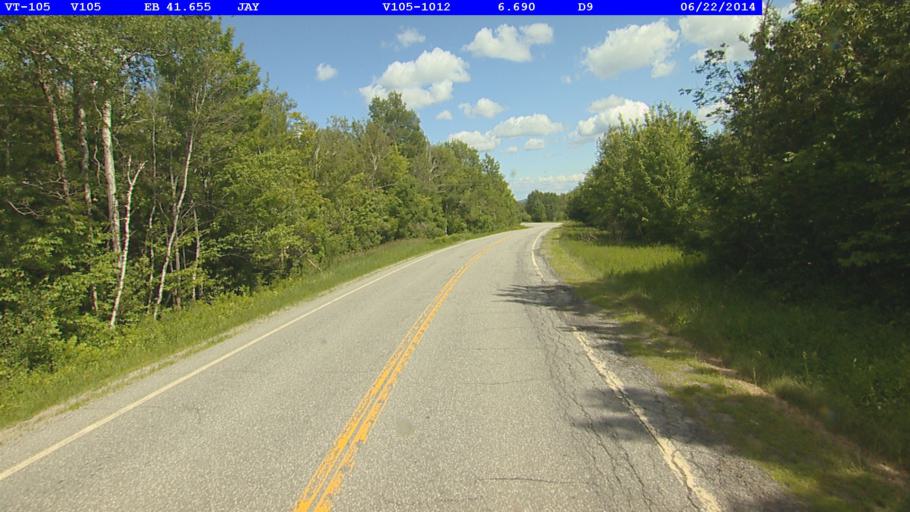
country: CA
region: Quebec
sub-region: Monteregie
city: Sutton
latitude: 44.9721
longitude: -72.4539
